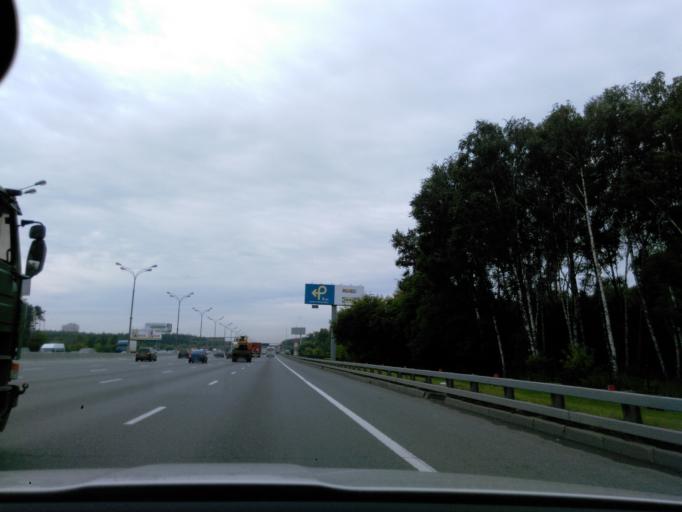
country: RU
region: Moscow
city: Zhulebino
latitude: 55.6743
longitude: 37.8352
